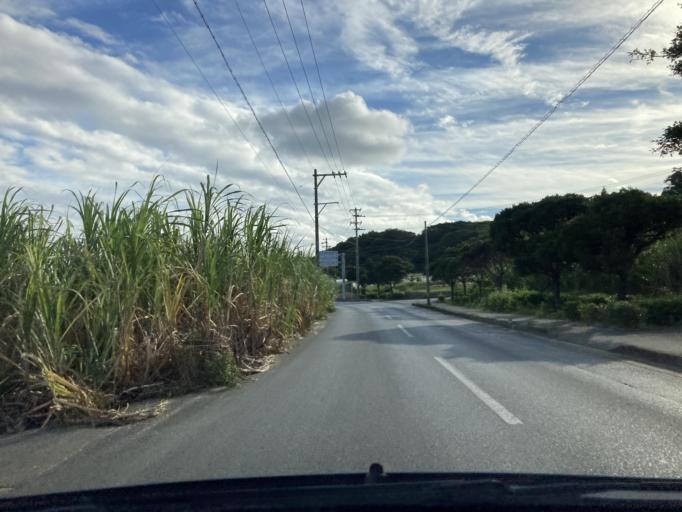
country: JP
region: Okinawa
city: Itoman
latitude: 26.1372
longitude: 127.7464
